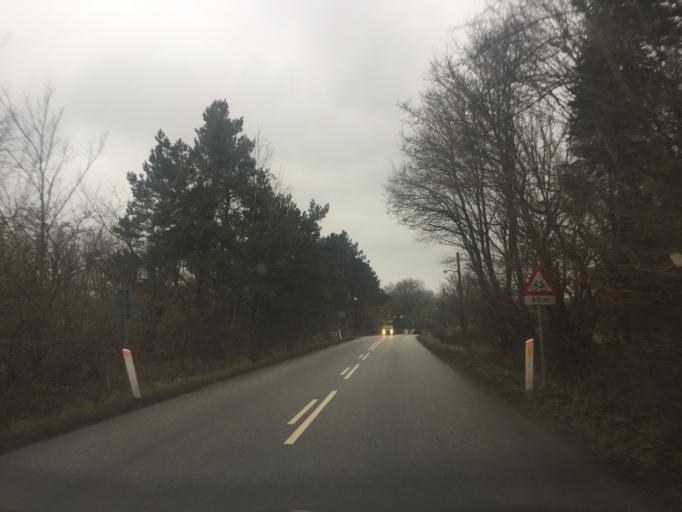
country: DK
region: Capital Region
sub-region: Albertslund Kommune
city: Albertslund
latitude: 55.6872
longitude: 12.3301
